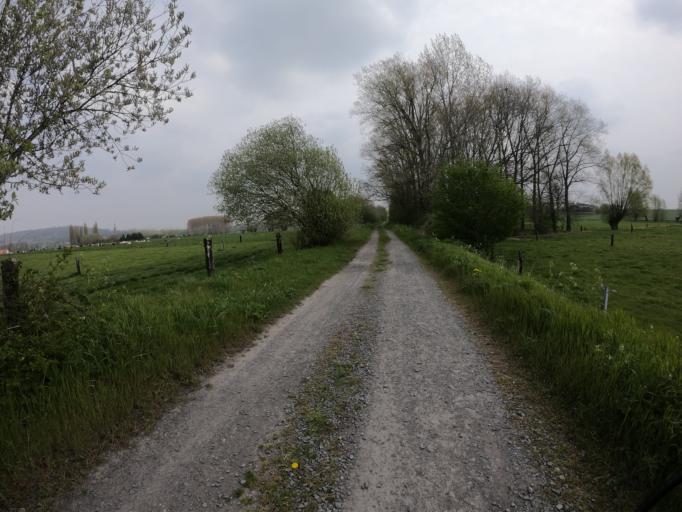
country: BE
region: Flanders
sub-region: Provincie Oost-Vlaanderen
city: Ronse
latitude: 50.7411
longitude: 3.5563
